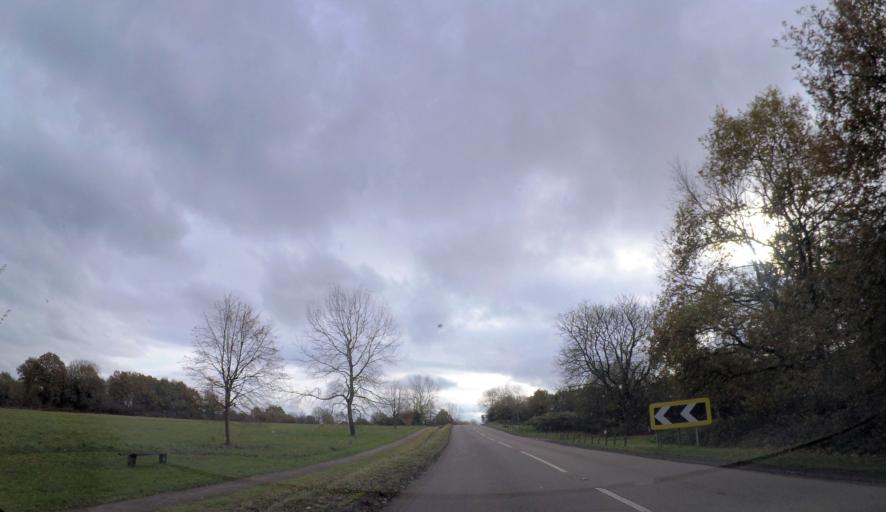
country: GB
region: England
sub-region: Surrey
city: Salfords
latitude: 51.2124
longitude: -0.1747
